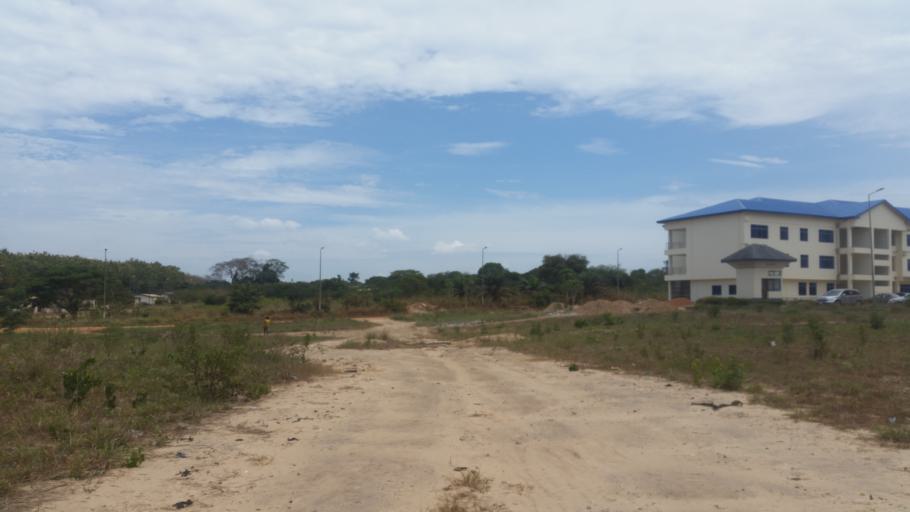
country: GH
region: Central
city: Cape Coast
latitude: 5.1219
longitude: -1.2958
